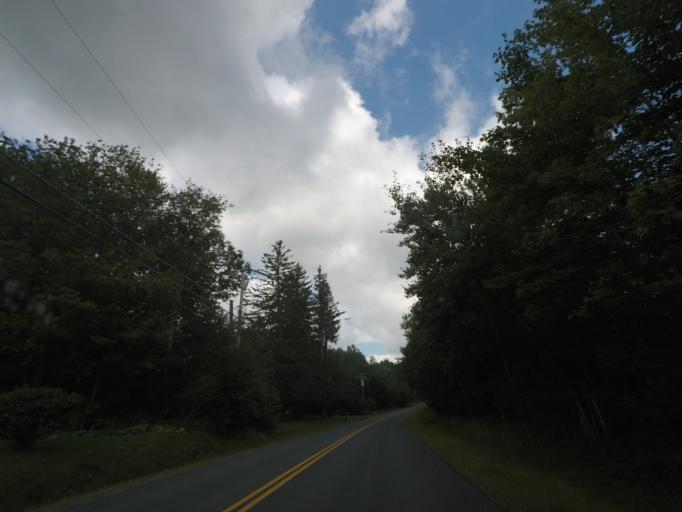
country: US
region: New York
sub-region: Rensselaer County
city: Averill Park
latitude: 42.6382
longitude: -73.4638
